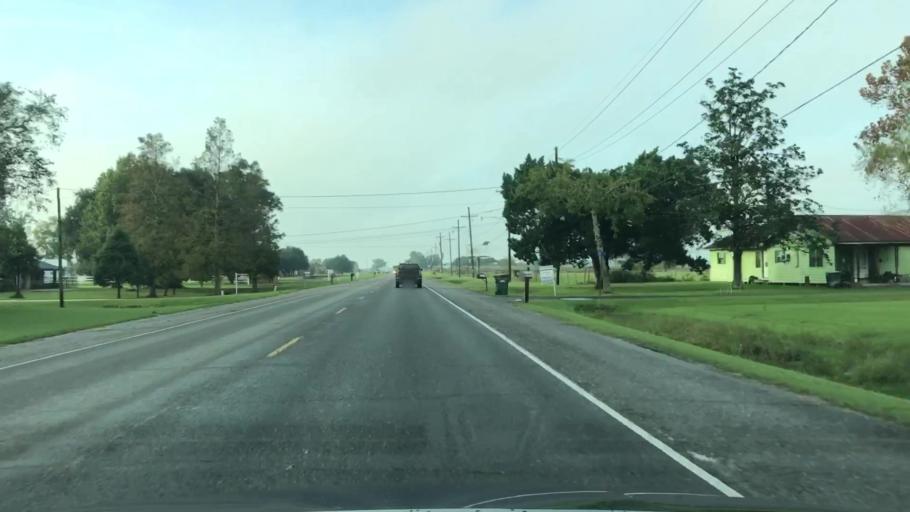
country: US
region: Louisiana
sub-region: Terrebonne Parish
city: Gray
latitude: 29.6701
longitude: -90.8168
